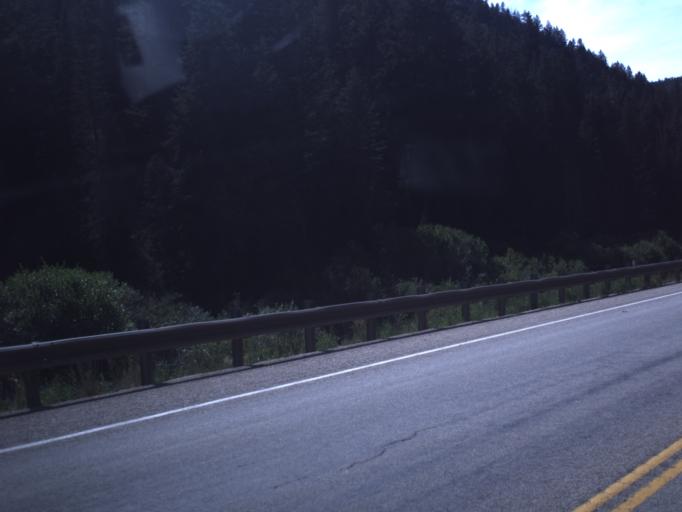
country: US
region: Utah
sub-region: Wasatch County
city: Heber
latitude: 40.3516
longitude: -111.2741
